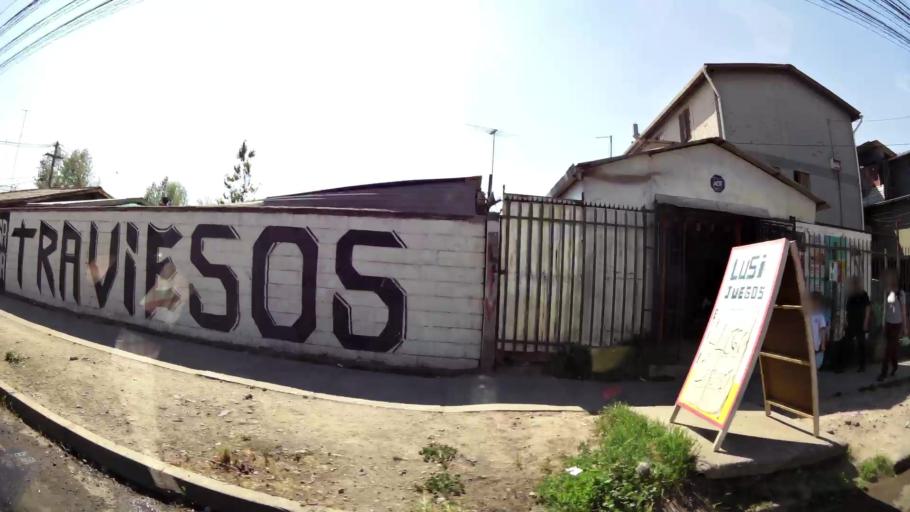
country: CL
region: Santiago Metropolitan
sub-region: Provincia de Cordillera
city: Puente Alto
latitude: -33.6228
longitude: -70.6074
